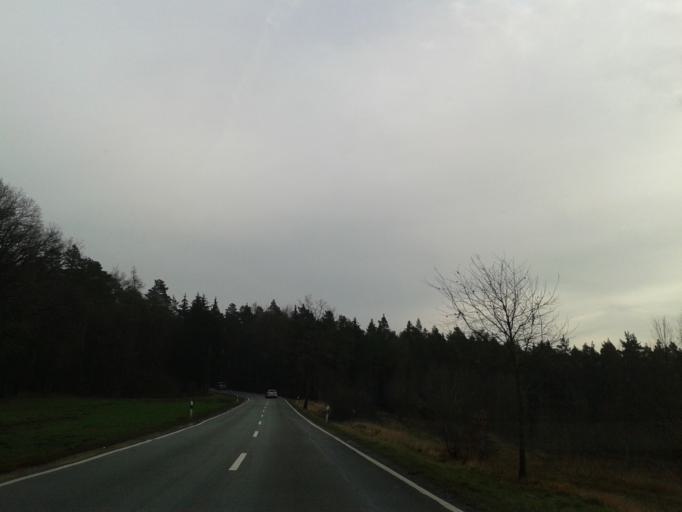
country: DE
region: Bavaria
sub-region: Upper Franconia
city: Weitramsdorf
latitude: 50.2320
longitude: 10.8829
